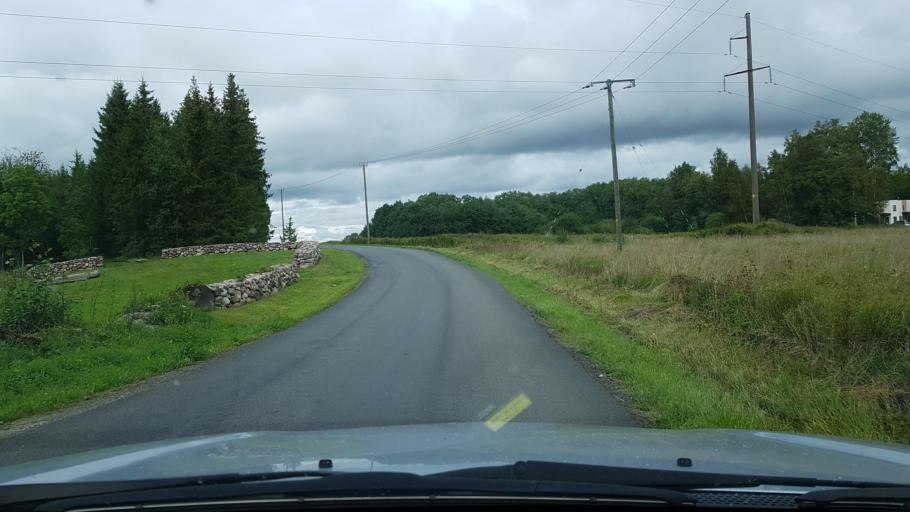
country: EE
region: Harju
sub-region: Rae vald
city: Vaida
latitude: 59.3482
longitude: 24.9613
